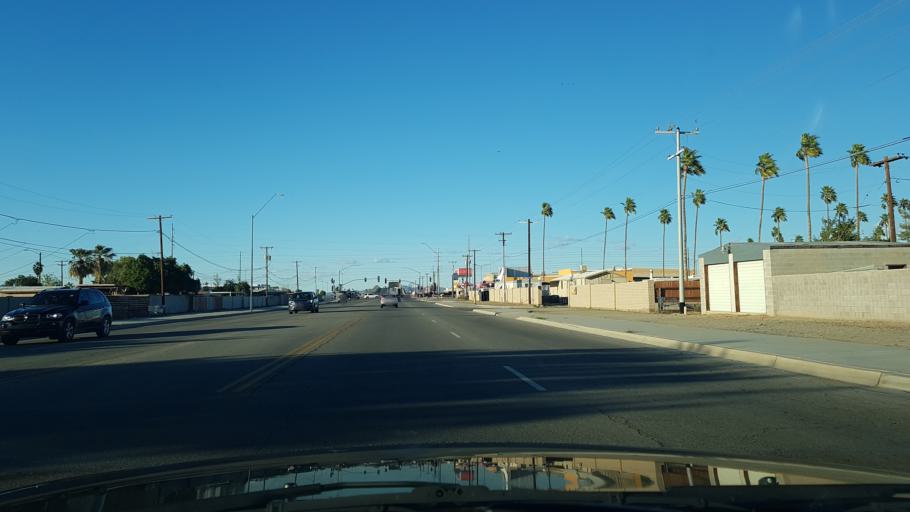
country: US
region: Arizona
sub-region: Yuma County
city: Yuma
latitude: 32.6818
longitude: -114.5988
